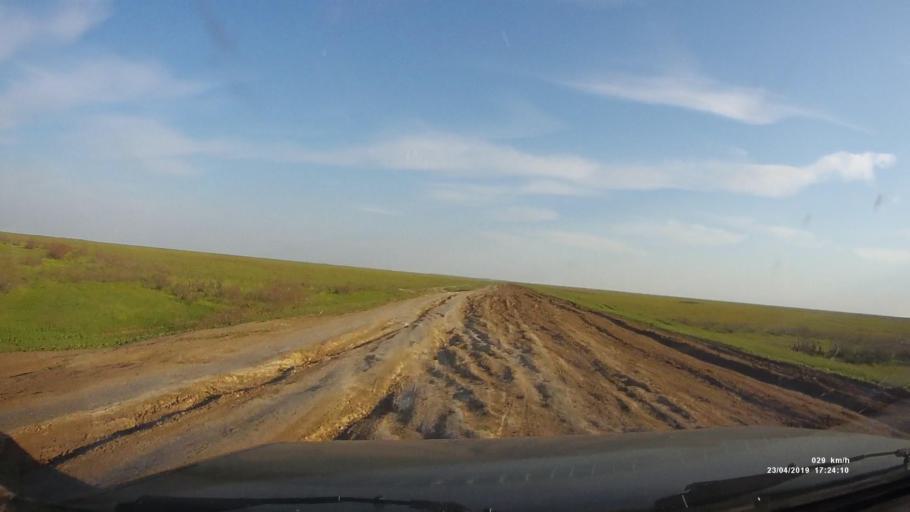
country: RU
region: Kalmykiya
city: Priyutnoye
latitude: 46.1581
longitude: 43.5084
